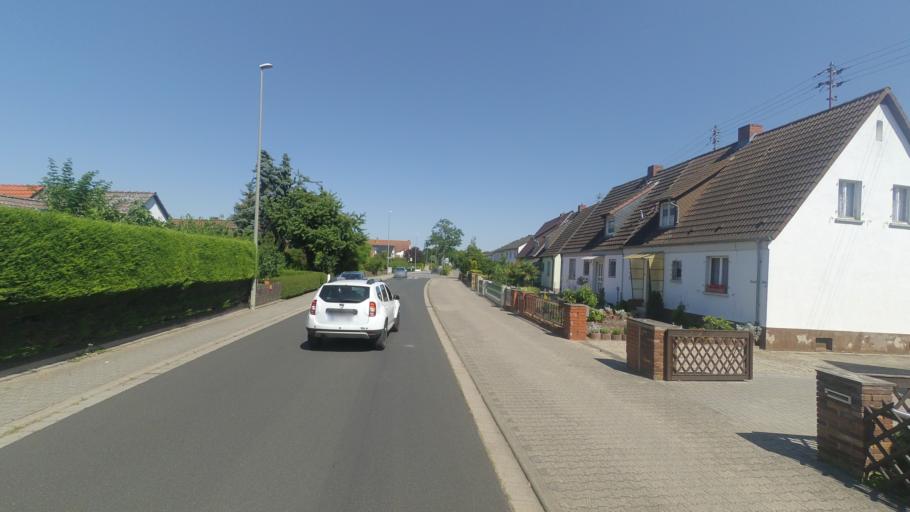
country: DE
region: Rheinland-Pfalz
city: Limburgerhof
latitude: 49.4226
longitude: 8.3994
